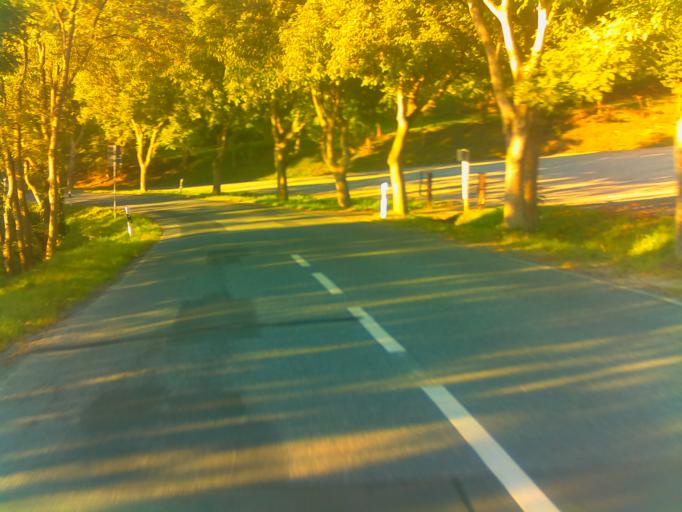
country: DE
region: Thuringia
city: Seitenroda
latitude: 50.8024
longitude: 11.6143
